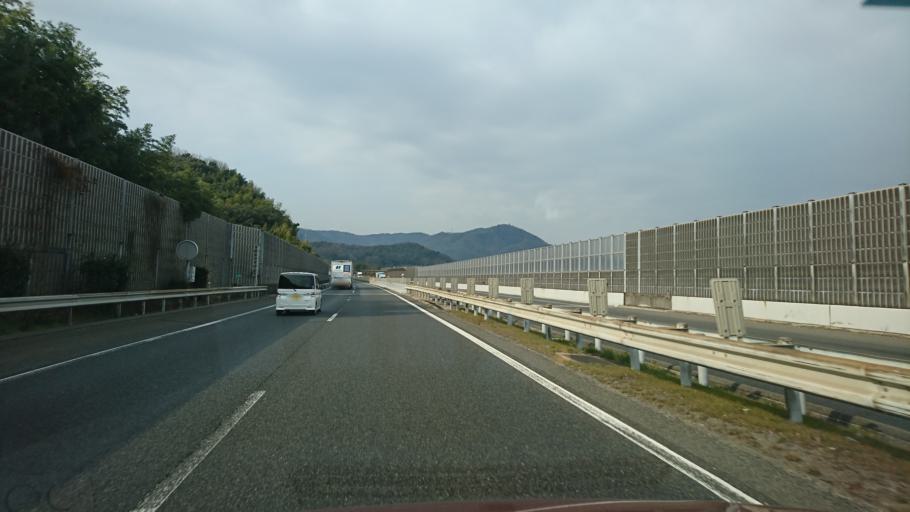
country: JP
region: Hiroshima
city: Fukuyama
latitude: 34.5170
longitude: 133.3758
